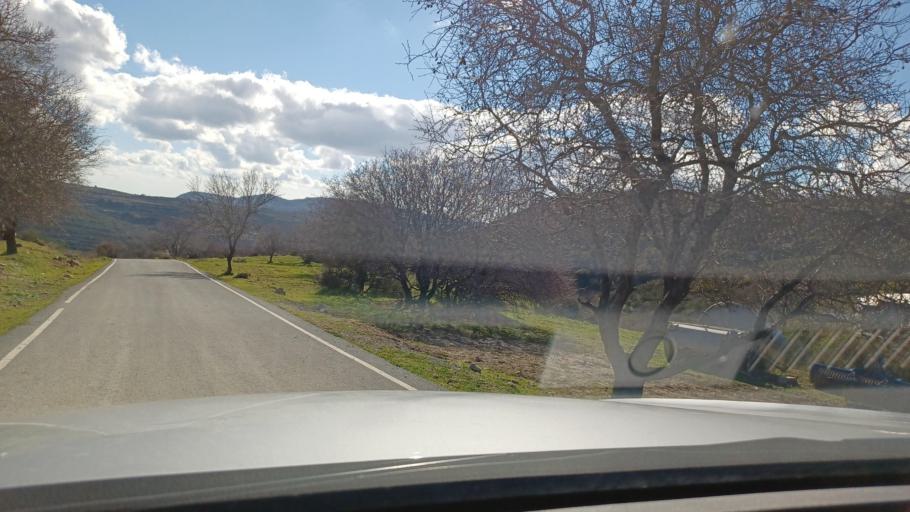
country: CY
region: Limassol
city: Pachna
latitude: 34.8274
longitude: 32.8065
